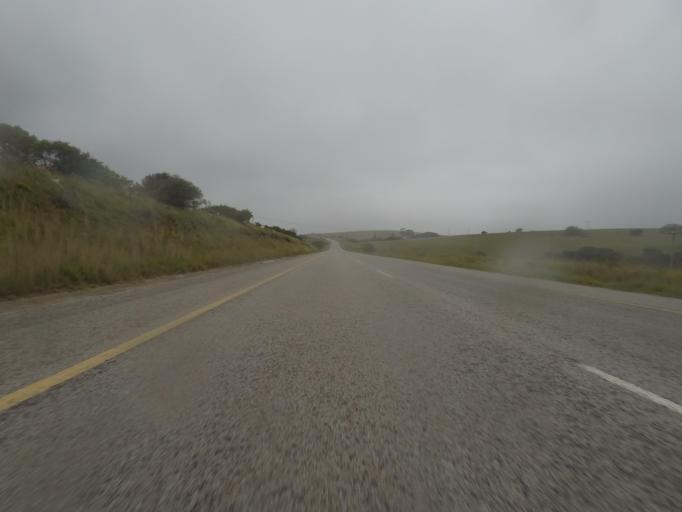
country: ZA
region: Eastern Cape
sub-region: Cacadu District Municipality
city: Grahamstown
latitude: -33.6326
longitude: 26.3157
